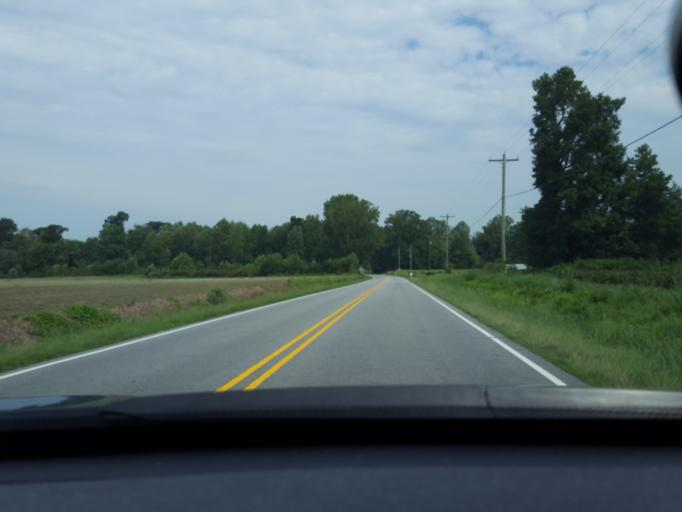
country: US
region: North Carolina
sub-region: Chowan County
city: Edenton
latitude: 36.1821
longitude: -76.6620
